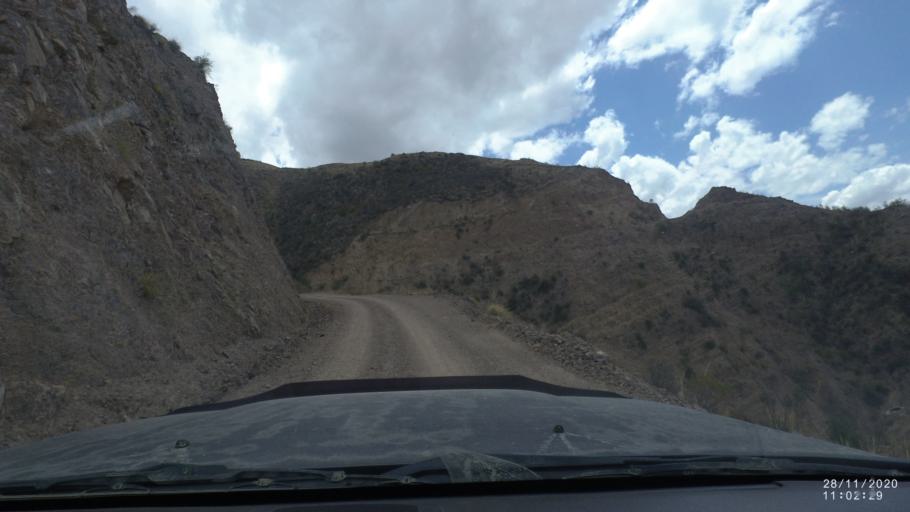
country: BO
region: Cochabamba
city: Capinota
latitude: -17.7661
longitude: -66.1042
